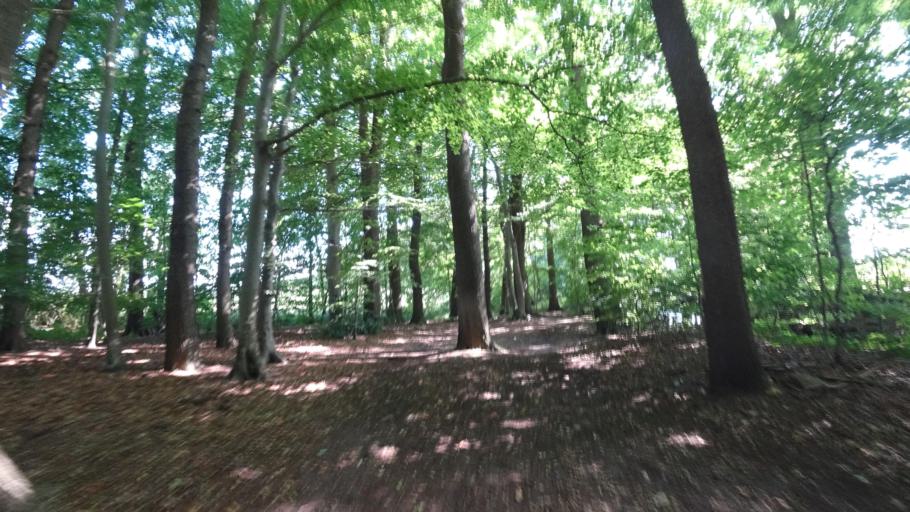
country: DE
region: North Rhine-Westphalia
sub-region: Regierungsbezirk Detmold
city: Guetersloh
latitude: 51.9423
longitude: 8.3929
